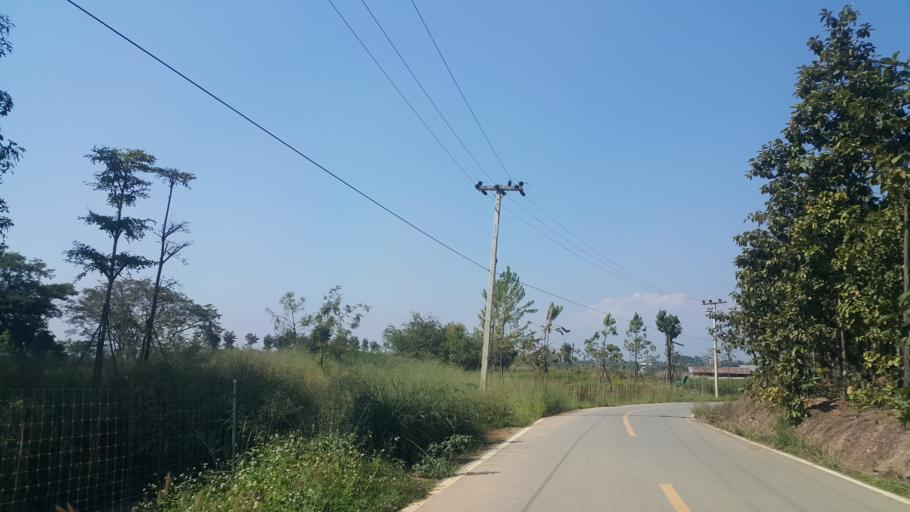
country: TH
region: Lamphun
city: Ban Thi
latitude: 18.6855
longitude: 99.1674
